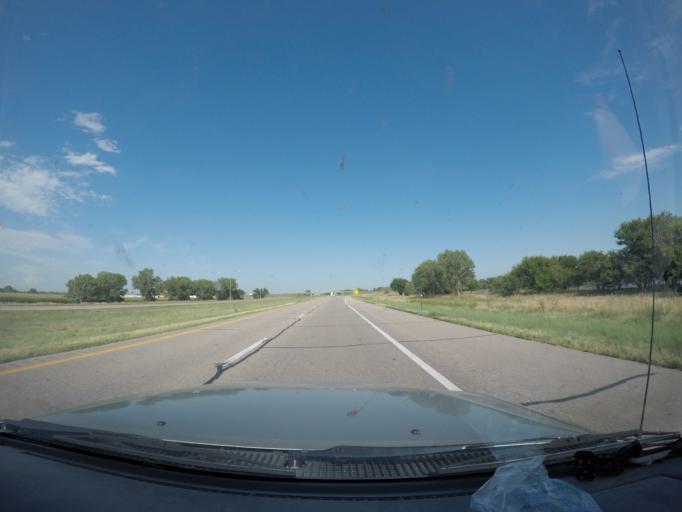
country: US
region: Nebraska
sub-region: Phelps County
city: Holdrege
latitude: 40.6900
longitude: -99.3870
